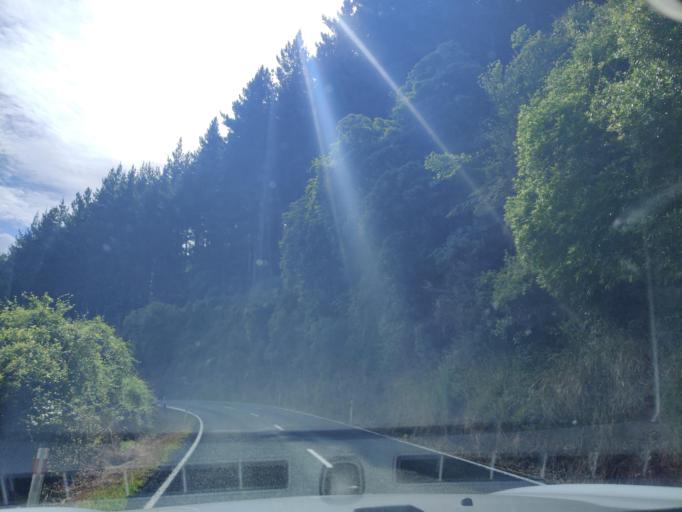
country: NZ
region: Waikato
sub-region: Otorohanga District
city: Otorohanga
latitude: -38.0979
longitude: 175.1278
